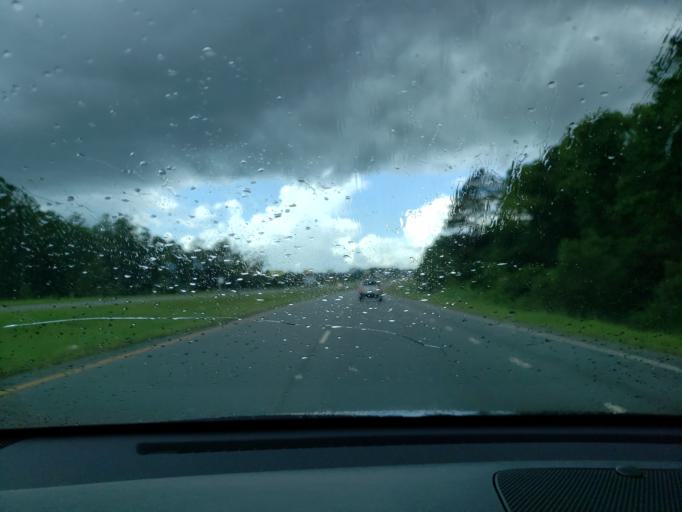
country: US
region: North Carolina
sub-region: Bladen County
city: Elizabethtown
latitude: 34.6038
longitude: -78.6192
